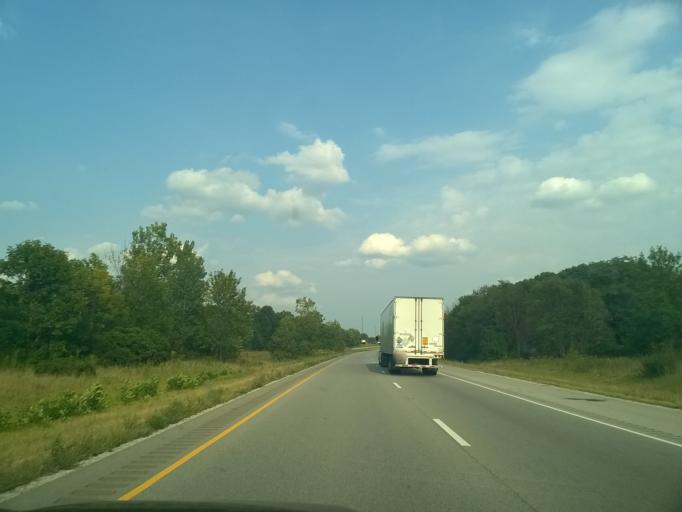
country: US
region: Indiana
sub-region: Vigo County
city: Seelyville
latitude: 39.4456
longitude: -87.2511
